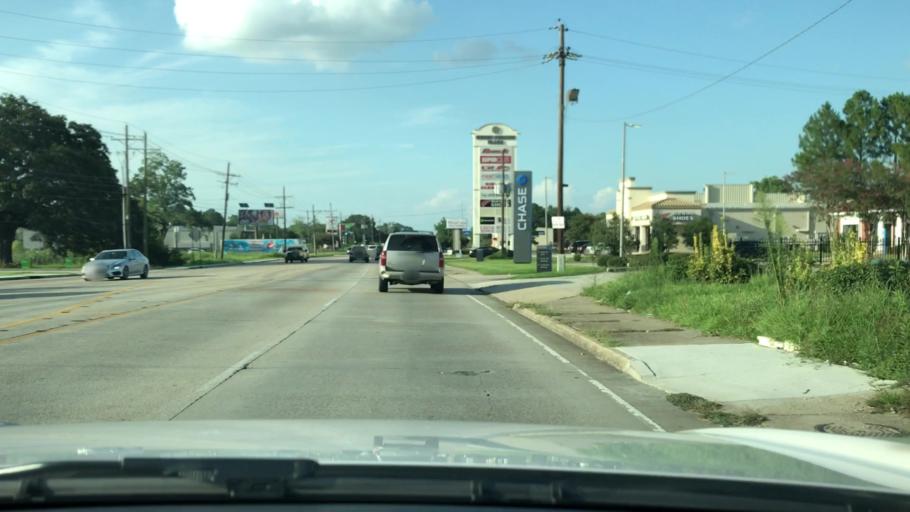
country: US
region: Louisiana
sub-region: East Baton Rouge Parish
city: Village Saint George
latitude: 30.3692
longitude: -91.0738
